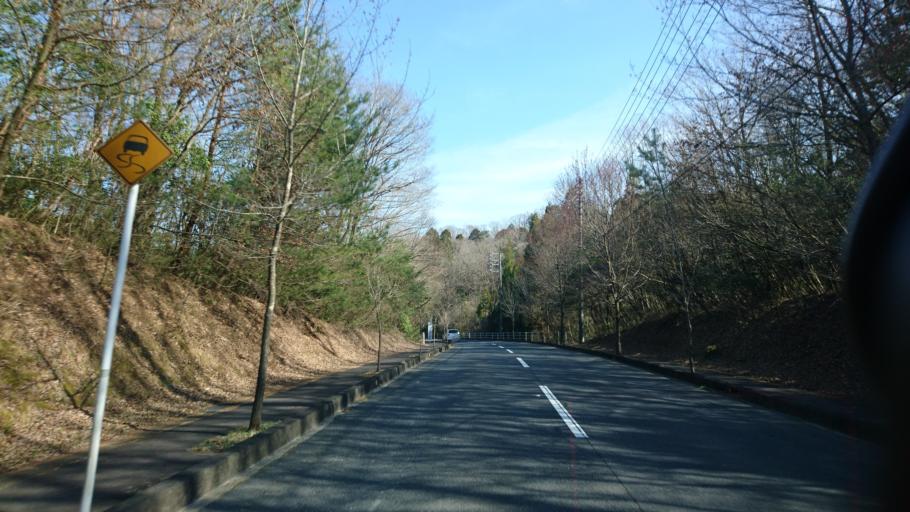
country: JP
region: Gifu
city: Nakatsugawa
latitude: 35.4631
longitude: 137.3930
